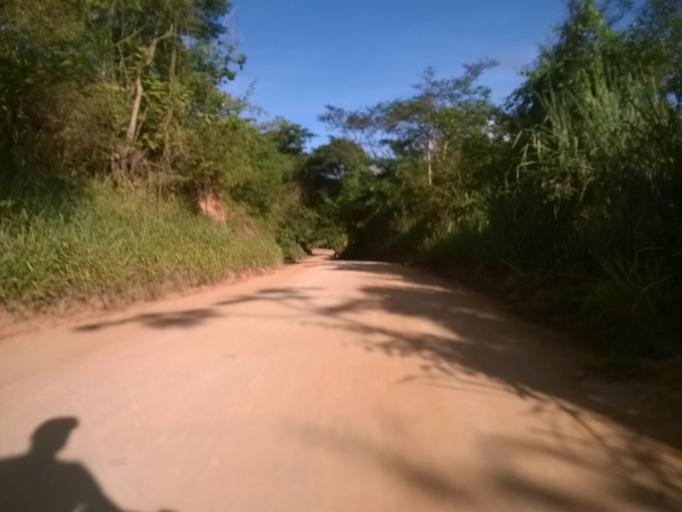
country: BR
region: Minas Gerais
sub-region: Uba
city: Uba
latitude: -21.0818
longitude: -42.9967
